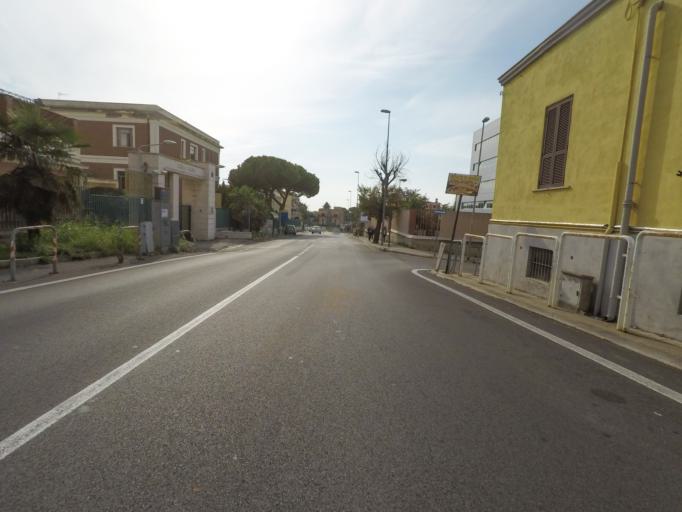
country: IT
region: Latium
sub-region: Citta metropolitana di Roma Capitale
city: Civitavecchia
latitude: 42.0999
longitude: 11.8009
